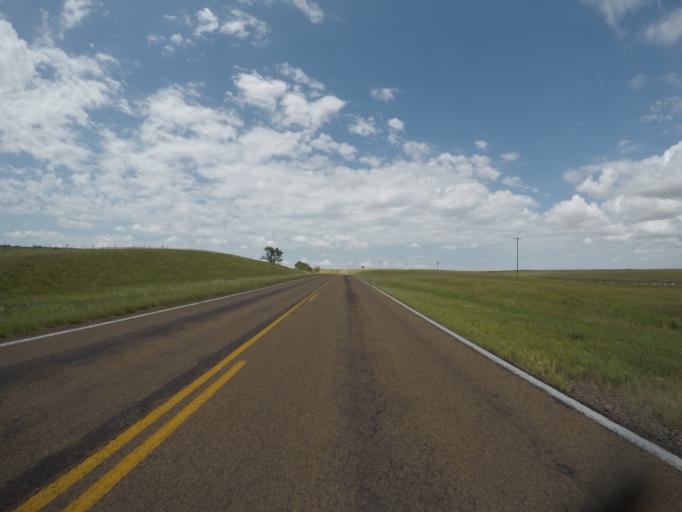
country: US
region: Kansas
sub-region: Rawlins County
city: Atwood
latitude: 39.9518
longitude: -101.0561
